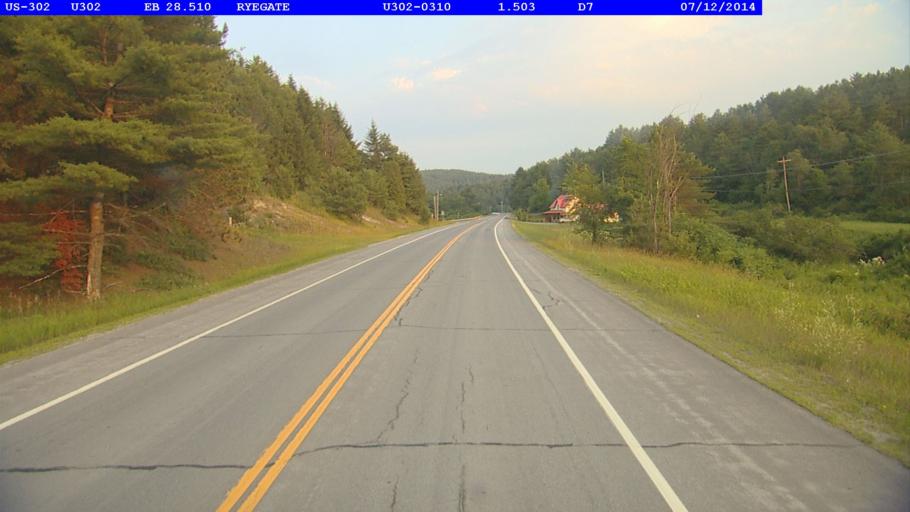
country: US
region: New Hampshire
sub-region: Grafton County
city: Woodsville
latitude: 44.1927
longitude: -72.1475
